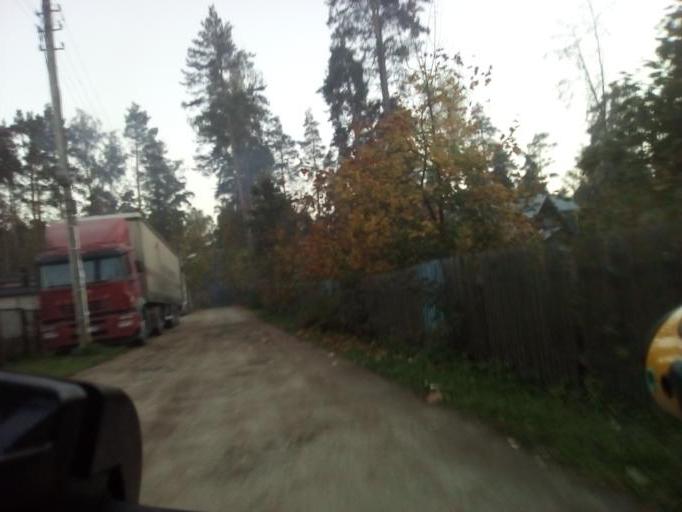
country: RU
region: Moskovskaya
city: Kratovo
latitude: 55.6040
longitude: 38.1591
